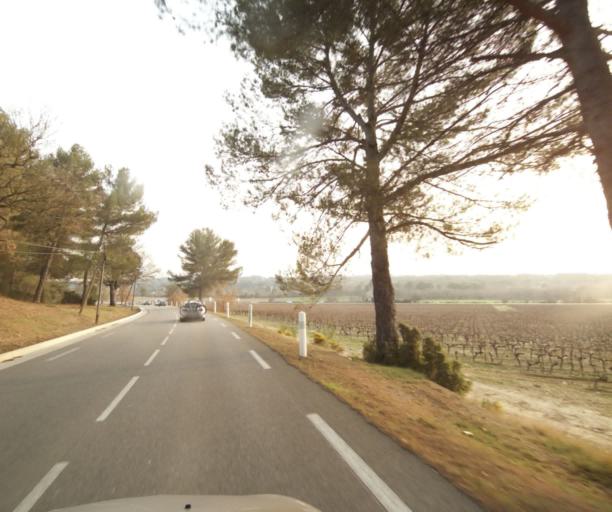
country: FR
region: Provence-Alpes-Cote d'Azur
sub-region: Departement des Bouches-du-Rhone
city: Eguilles
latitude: 43.5902
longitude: 5.3674
